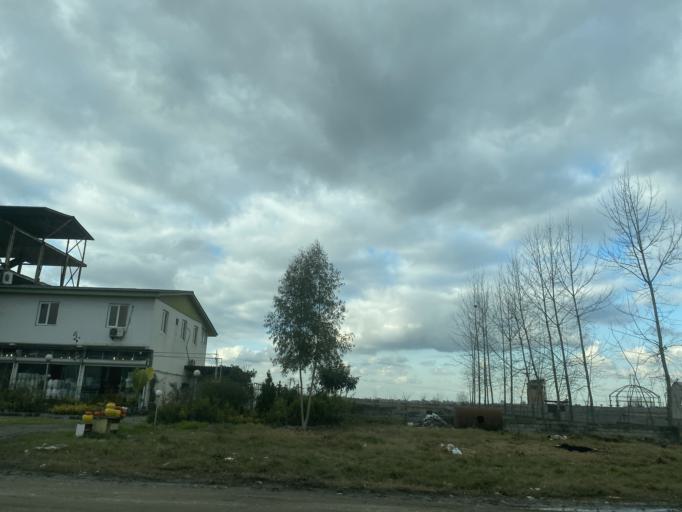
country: IR
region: Mazandaran
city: Amol
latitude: 36.4365
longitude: 52.3726
